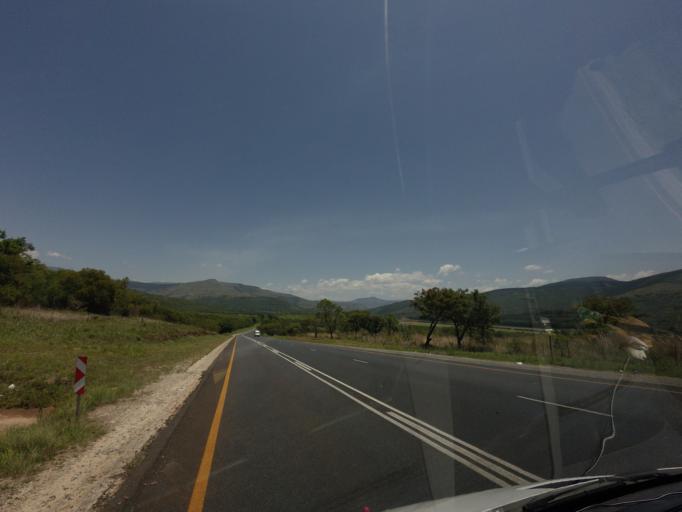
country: ZA
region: Mpumalanga
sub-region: Ehlanzeni District
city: Nelspruit
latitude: -25.4556
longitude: 30.6762
